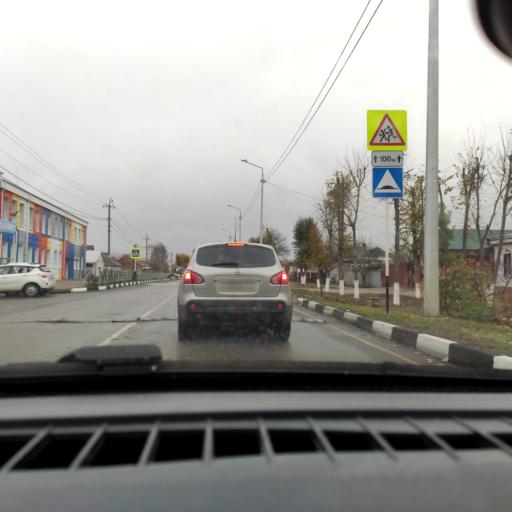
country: RU
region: Belgorod
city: Alekseyevka
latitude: 50.6317
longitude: 38.7029
